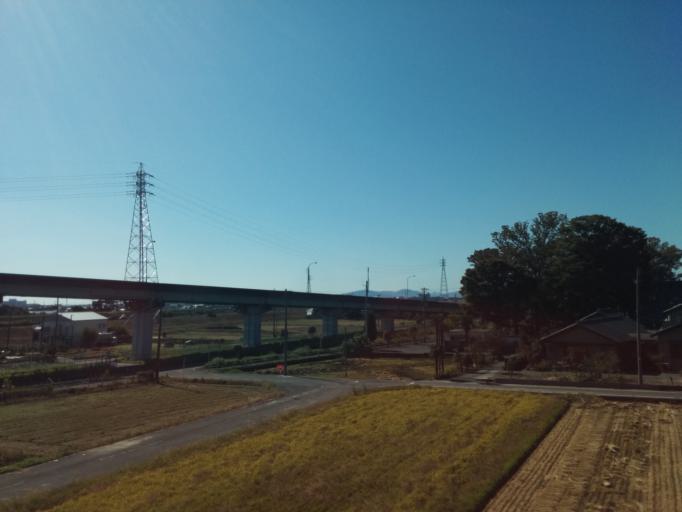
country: JP
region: Aichi
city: Kozakai-cho
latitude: 34.7883
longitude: 137.3525
